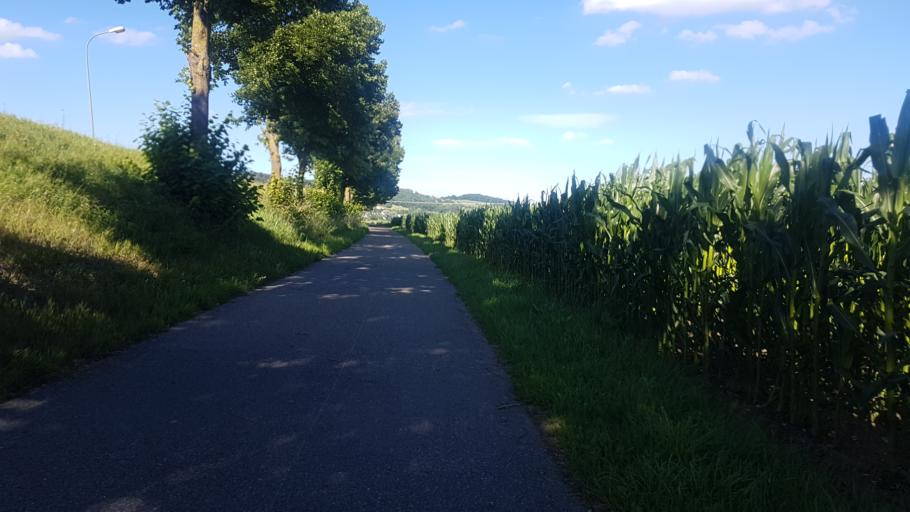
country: DE
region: Bavaria
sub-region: Swabia
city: Donauwoerth
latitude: 48.7147
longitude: 10.8014
